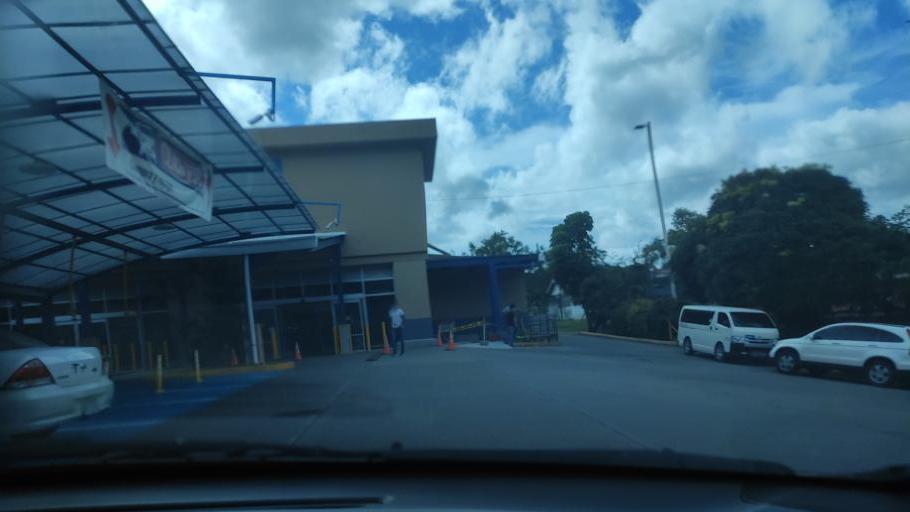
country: PA
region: Panama
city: Panama
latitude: 9.0155
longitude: -79.5362
